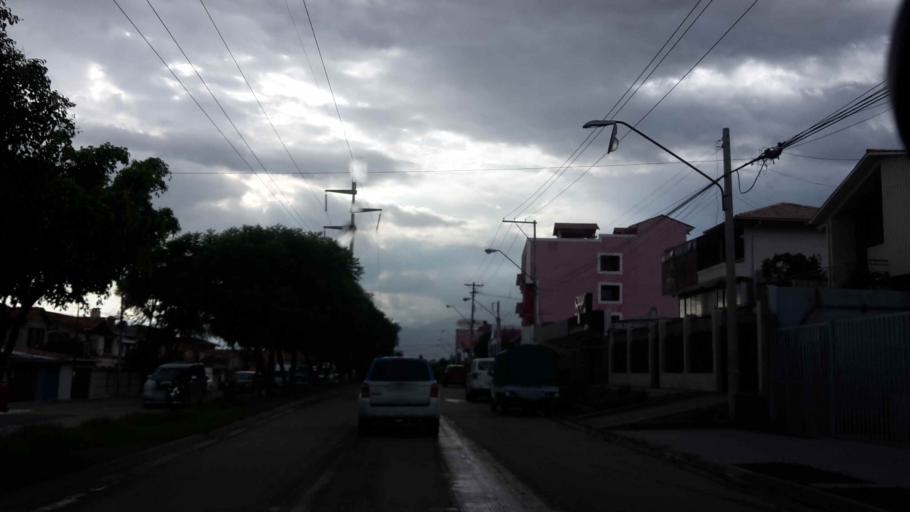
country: BO
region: Cochabamba
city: Cochabamba
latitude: -17.3653
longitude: -66.1586
